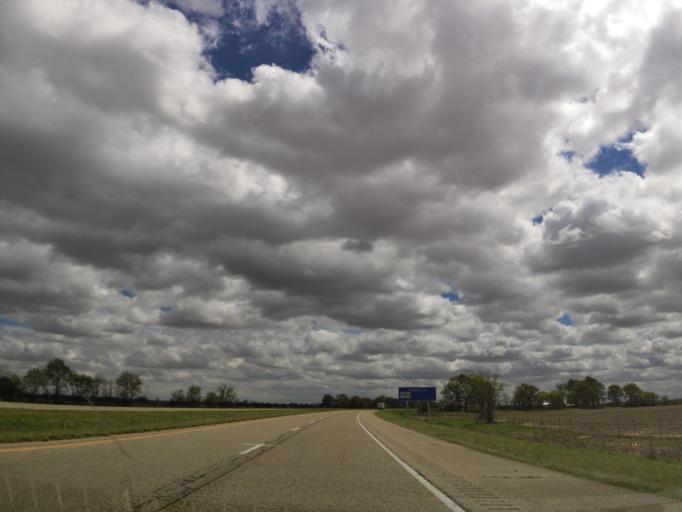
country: US
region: Arkansas
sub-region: Poinsett County
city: Trumann
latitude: 35.6456
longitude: -90.5160
